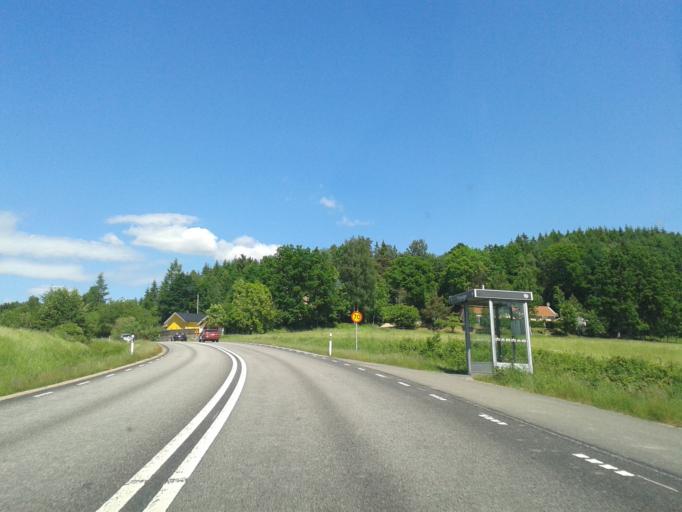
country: SE
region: Vaestra Goetaland
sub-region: Orust
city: Henan
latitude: 58.3282
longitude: 11.6891
